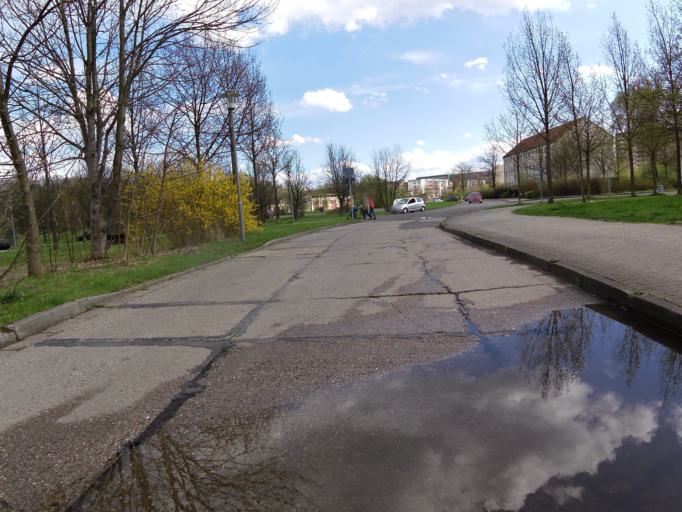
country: DE
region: Saxony
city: Markranstadt
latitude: 51.3261
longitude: 12.2889
